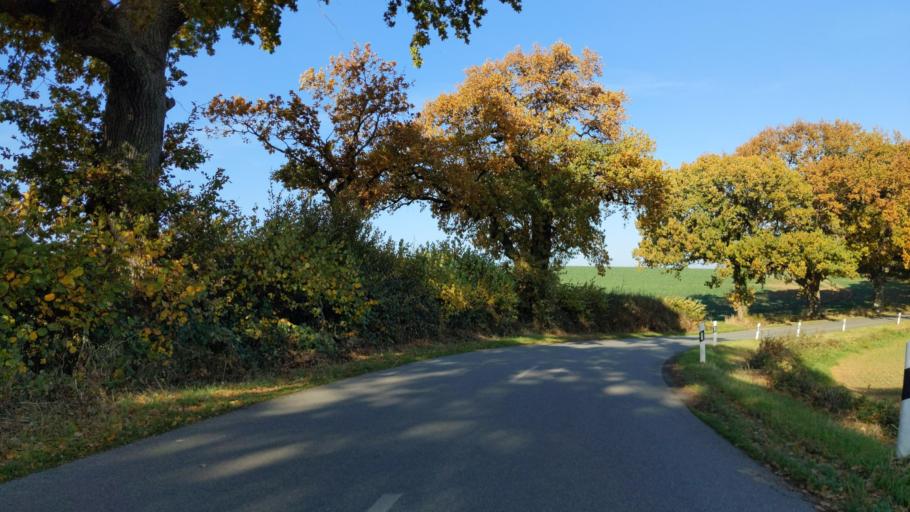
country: DE
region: Schleswig-Holstein
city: Neustadt in Holstein
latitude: 54.1158
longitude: 10.7767
